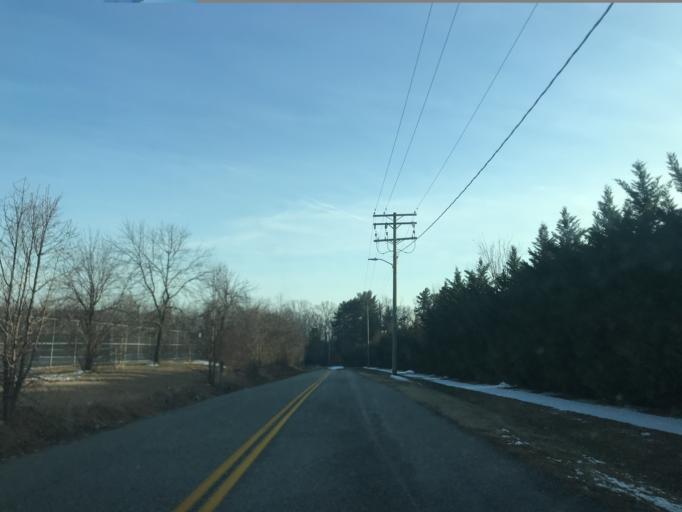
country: US
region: Maryland
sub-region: Harford County
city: Edgewood
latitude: 39.4072
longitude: -76.3315
